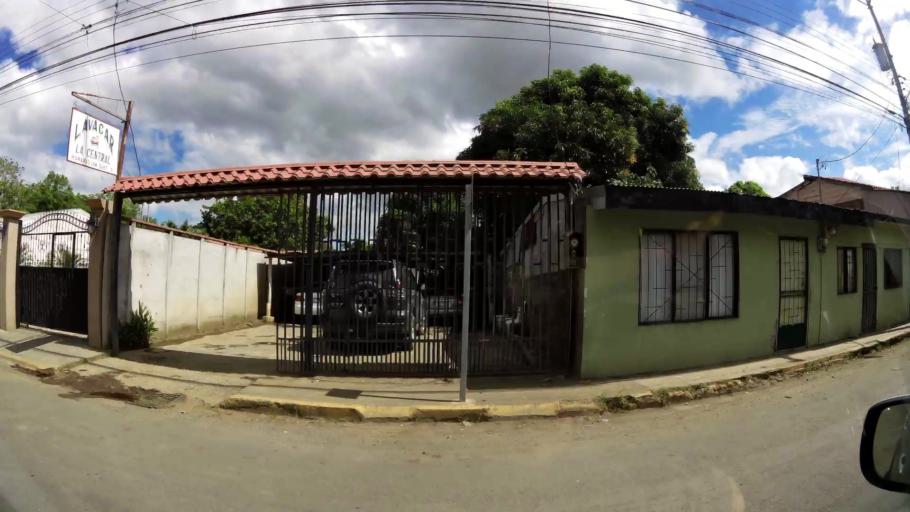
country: CR
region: Guanacaste
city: Santa Cruz
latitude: 10.2601
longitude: -85.5841
